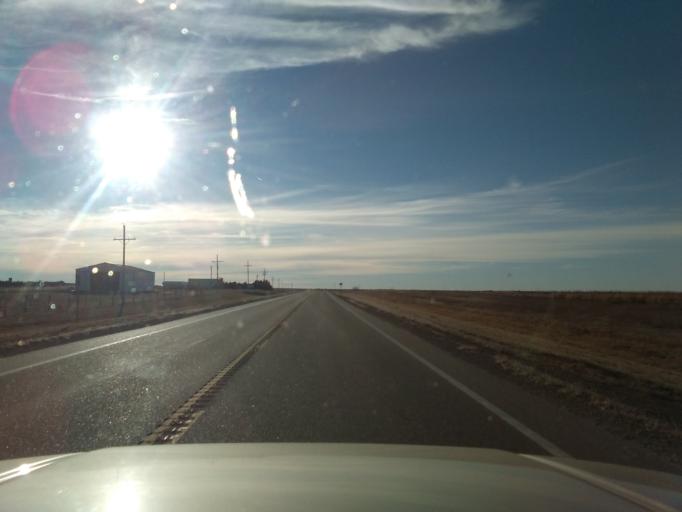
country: US
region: Kansas
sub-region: Sheridan County
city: Hoxie
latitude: 39.5379
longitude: -100.5824
